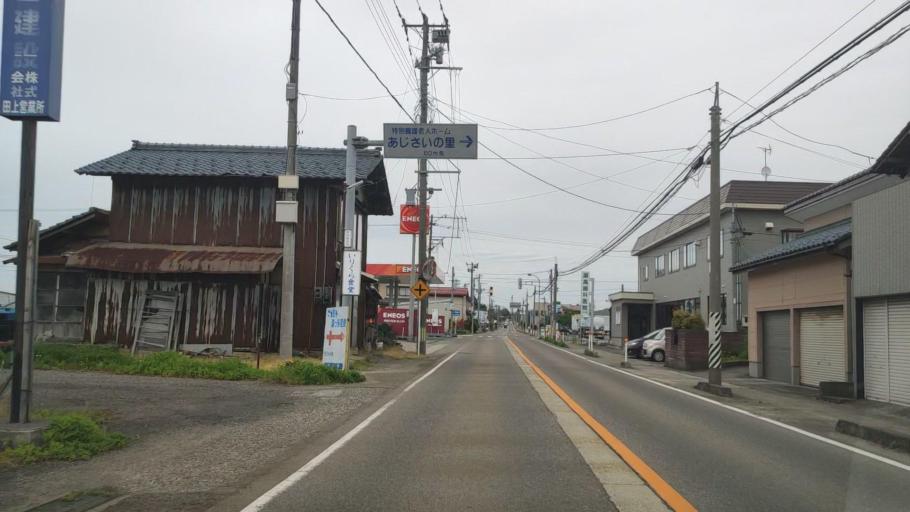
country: JP
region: Niigata
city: Kamo
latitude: 37.7193
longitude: 139.0753
